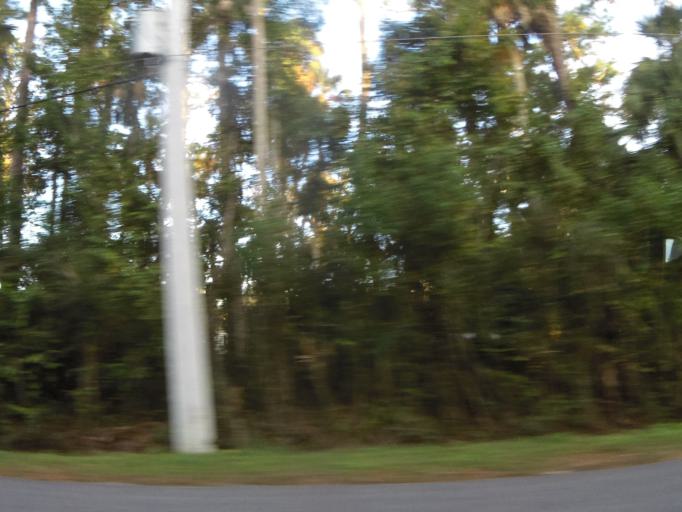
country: US
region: Florida
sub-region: Saint Johns County
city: Palm Valley
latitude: 30.1610
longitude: -81.3964
